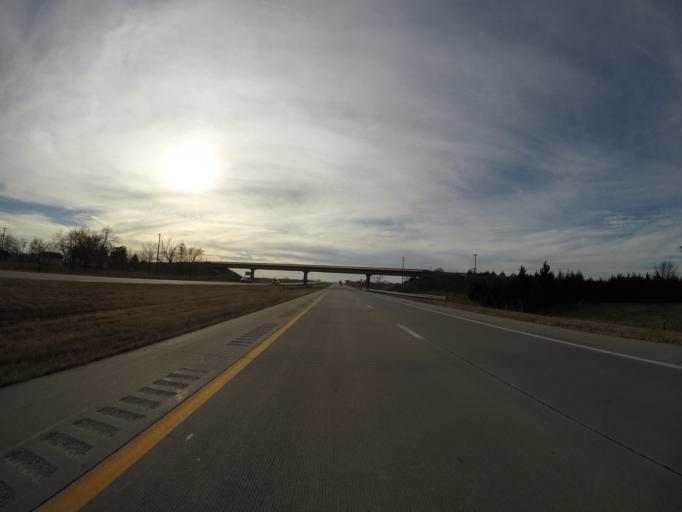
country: US
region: Kansas
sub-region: Franklin County
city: Wellsville
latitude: 38.7023
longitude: -95.0832
